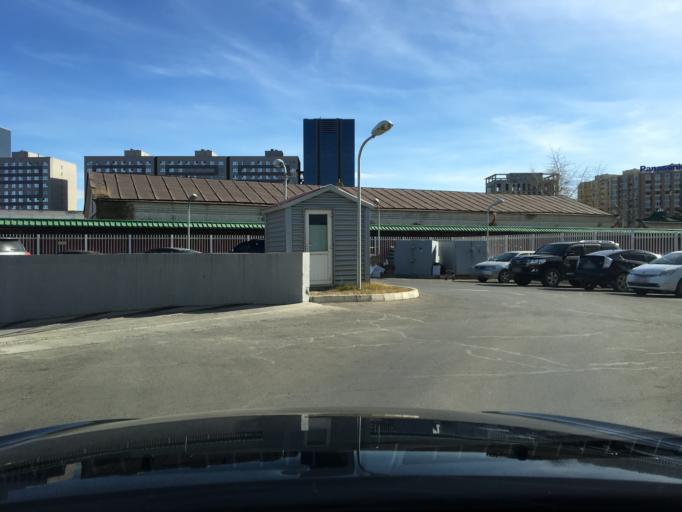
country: MN
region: Ulaanbaatar
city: Ulaanbaatar
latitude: 47.8982
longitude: 106.9057
